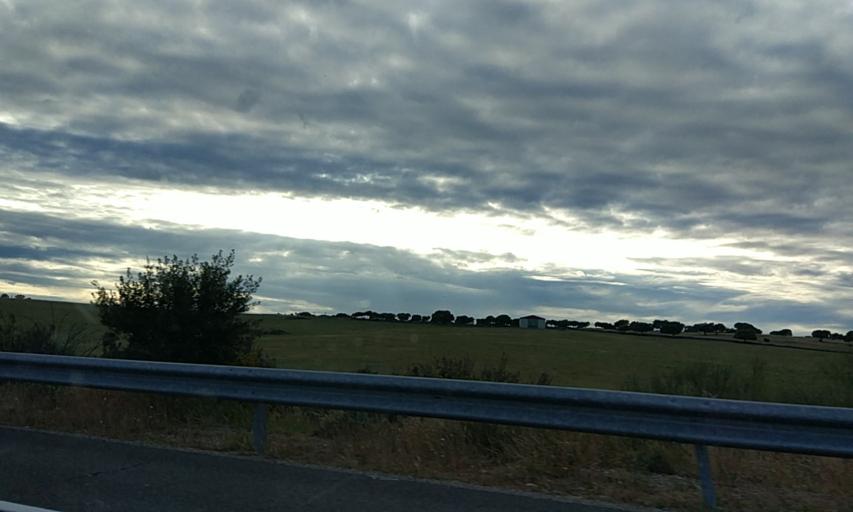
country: ES
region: Extremadura
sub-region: Provincia de Caceres
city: Casar de Caceres
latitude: 39.5331
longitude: -6.4129
